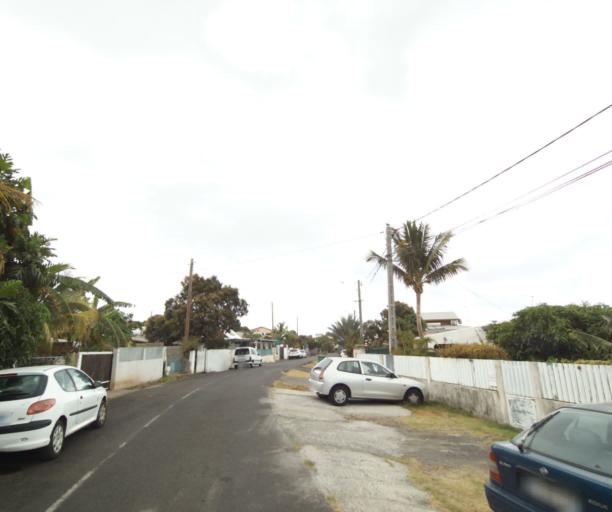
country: RE
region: Reunion
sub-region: Reunion
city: Saint-Paul
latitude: -21.0546
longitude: 55.2345
